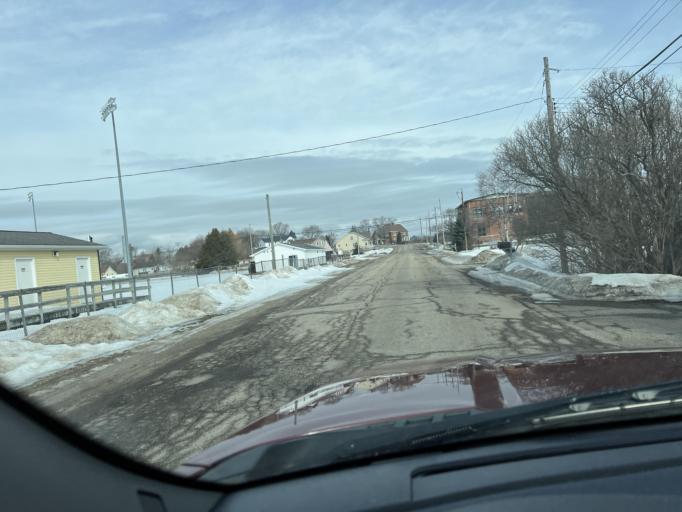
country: US
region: Michigan
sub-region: Mackinac County
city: Saint Ignace
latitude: 45.8645
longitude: -84.7244
